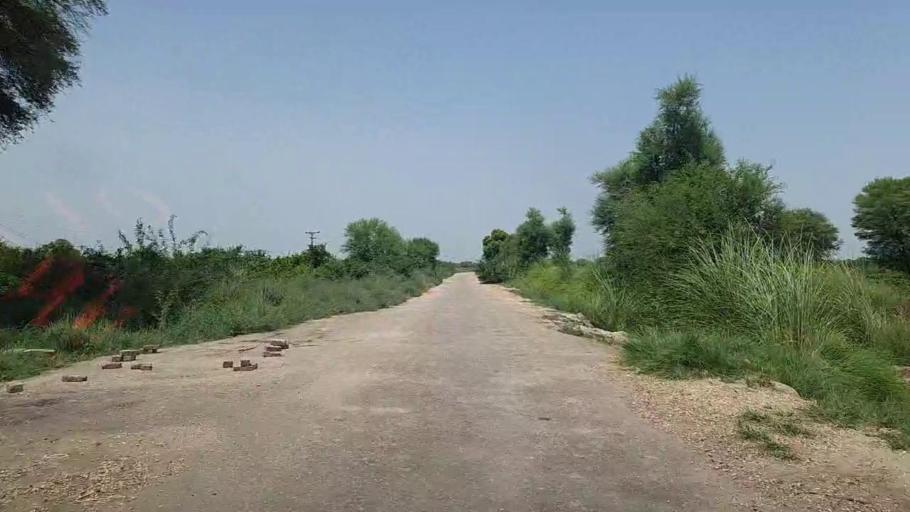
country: PK
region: Sindh
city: Pad Idan
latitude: 26.7442
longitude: 68.3140
